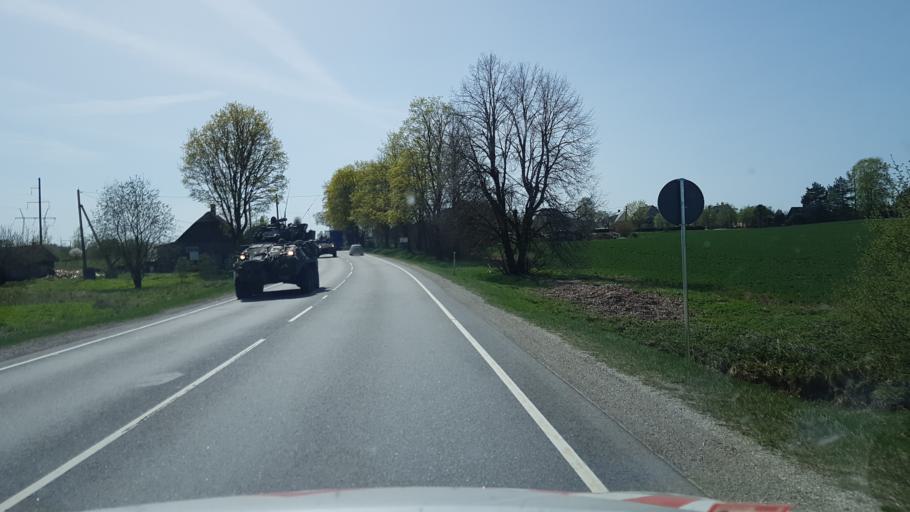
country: EE
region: Tartu
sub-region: Elva linn
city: Elva
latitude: 58.1499
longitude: 26.2605
